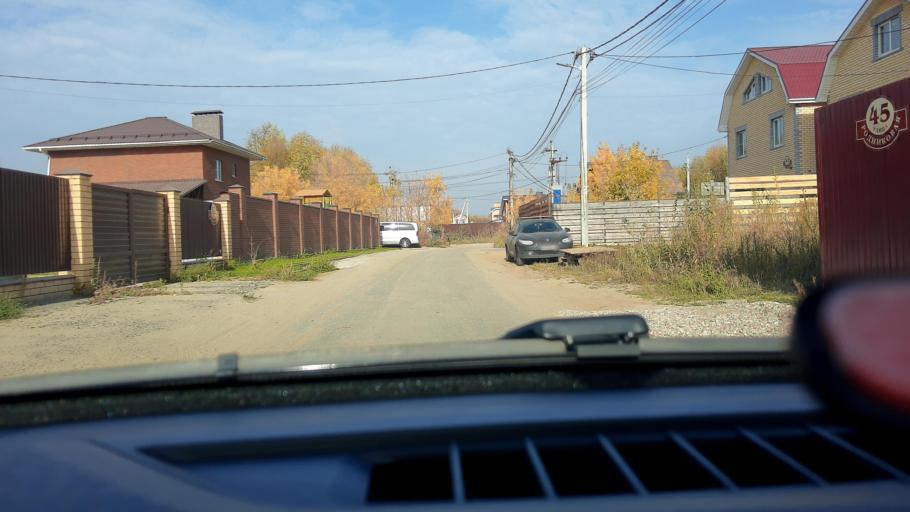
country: RU
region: Nizjnij Novgorod
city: Afonino
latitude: 56.2723
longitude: 44.1000
